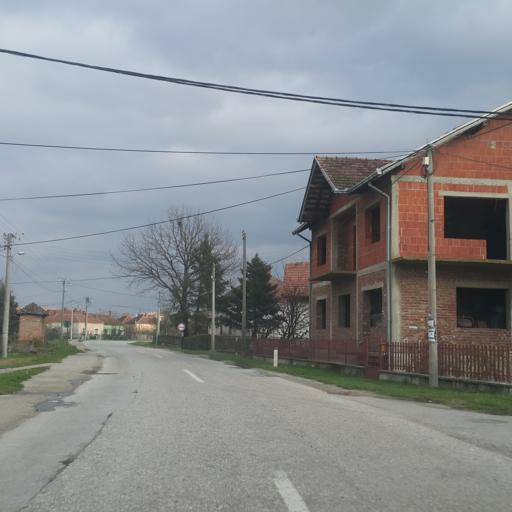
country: RS
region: Central Serbia
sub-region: Sumadijski Okrug
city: Lapovo
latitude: 44.2373
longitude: 21.1073
